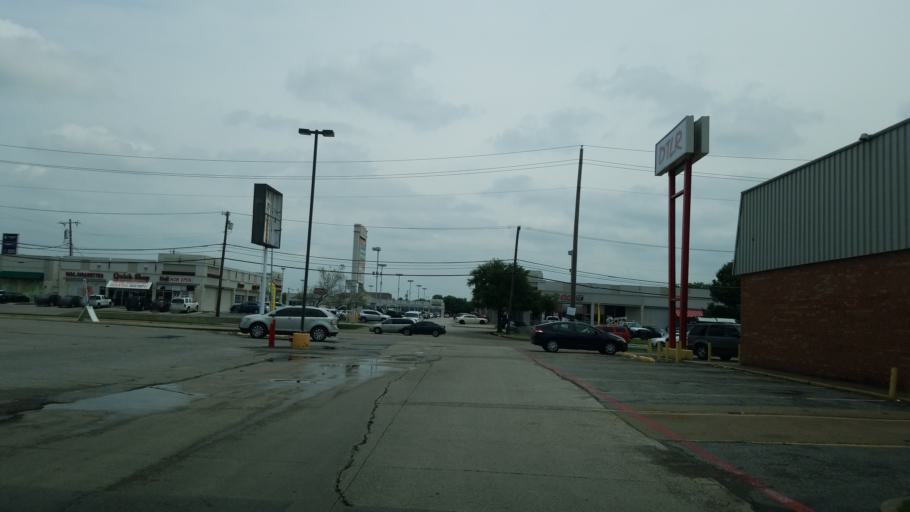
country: US
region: Texas
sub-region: Dallas County
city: Farmers Branch
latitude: 32.9086
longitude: -96.8729
